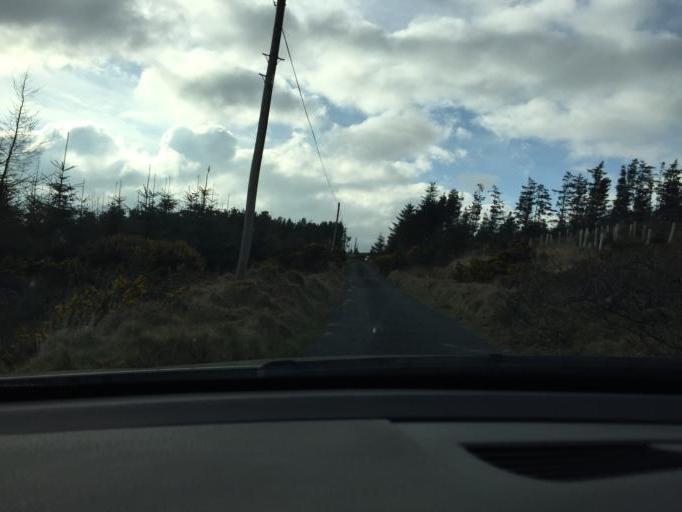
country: IE
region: Leinster
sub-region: Wicklow
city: Valleymount
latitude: 53.0723
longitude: -6.4879
